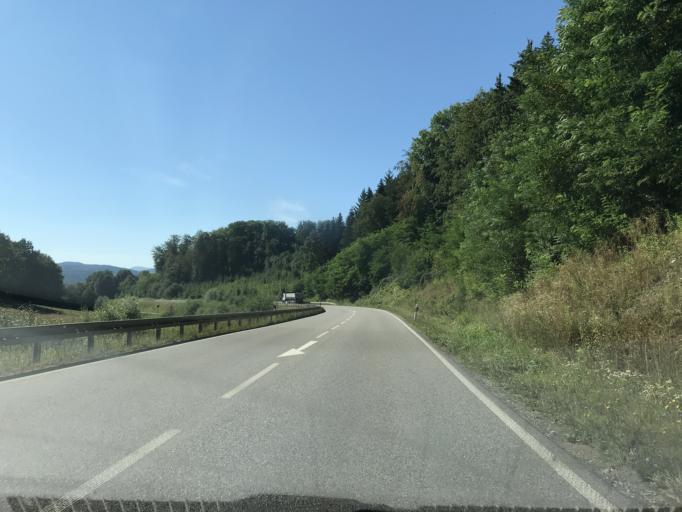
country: DE
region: Baden-Wuerttemberg
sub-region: Freiburg Region
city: Rheinfelden (Baden)
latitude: 47.5825
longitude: 7.7913
